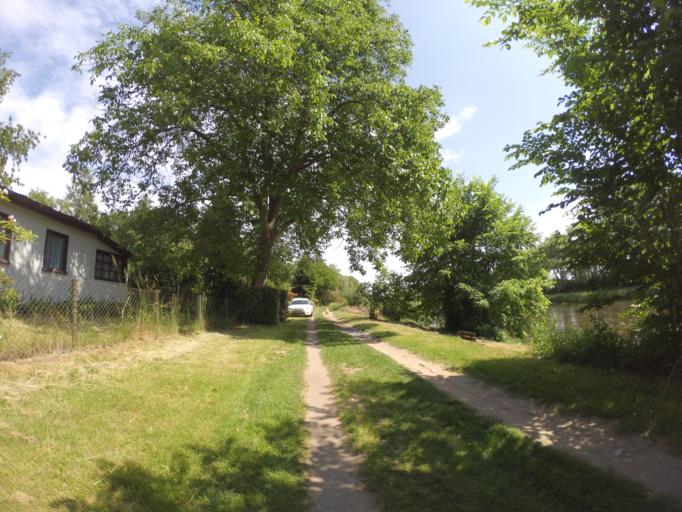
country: CZ
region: Central Bohemia
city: Milovice
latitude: 50.1718
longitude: 14.9025
